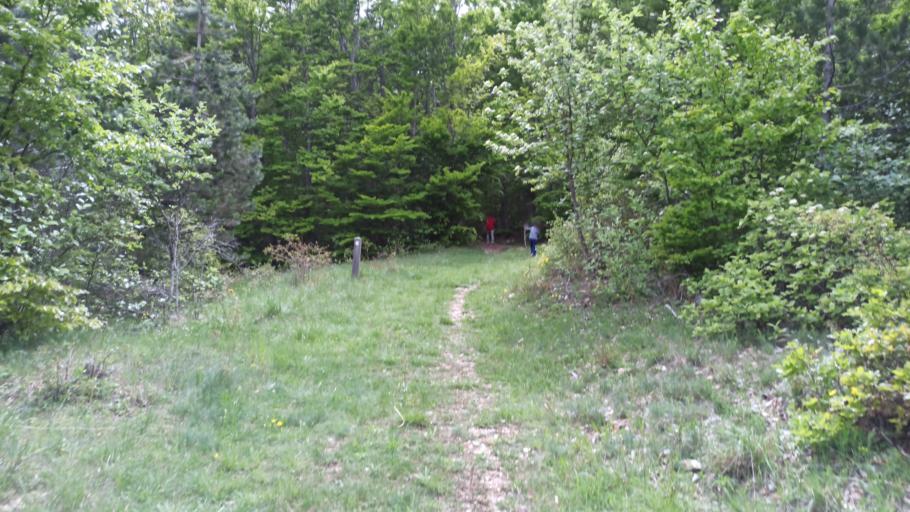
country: FR
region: Provence-Alpes-Cote d'Azur
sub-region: Departement du Vaucluse
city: Sault
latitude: 44.1418
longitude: 5.3458
